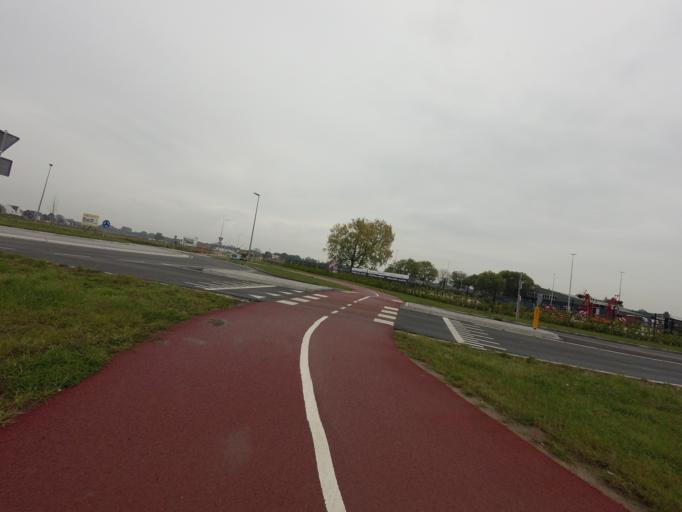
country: NL
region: Utrecht
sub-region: Gemeente Vianen
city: Vianen
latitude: 51.9835
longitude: 5.1137
